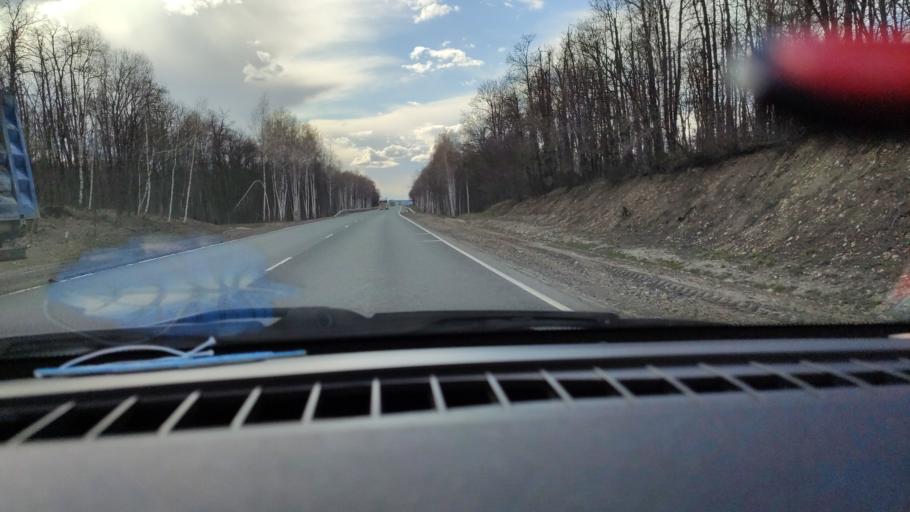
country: RU
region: Saratov
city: Vol'sk
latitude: 52.1118
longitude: 47.3292
